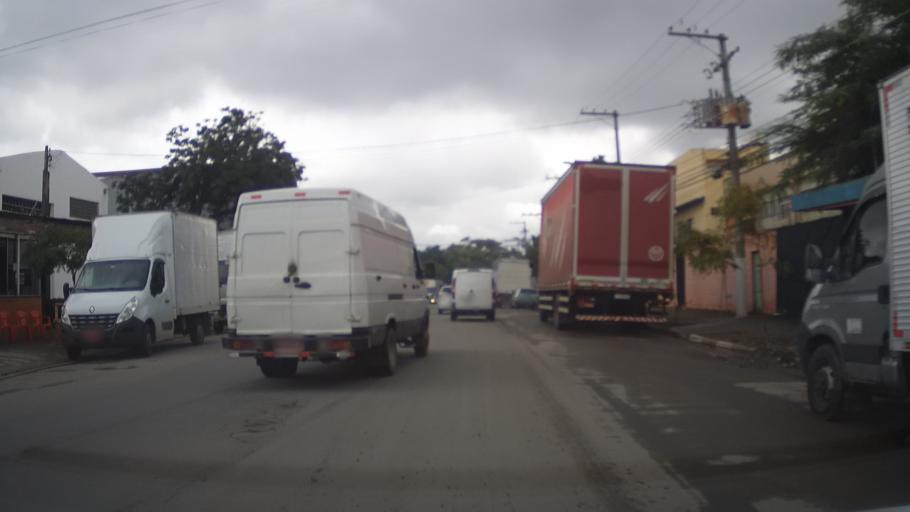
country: BR
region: Sao Paulo
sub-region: Guarulhos
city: Guarulhos
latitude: -23.4629
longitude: -46.4828
